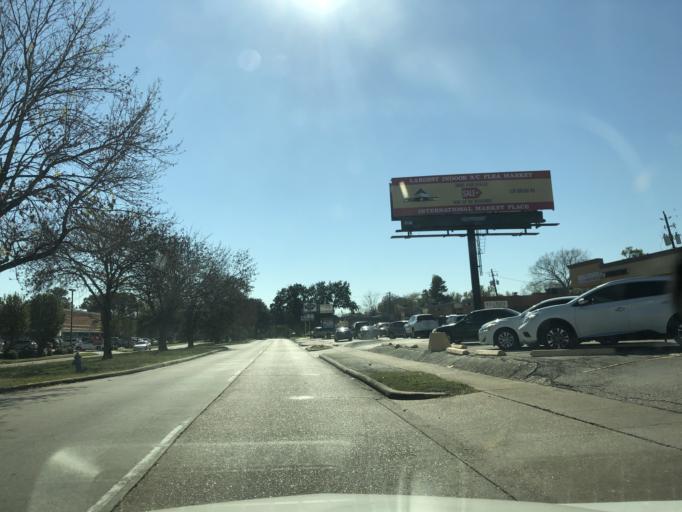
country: US
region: Texas
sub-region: Harris County
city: Bellaire
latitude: 29.6935
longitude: -95.4931
